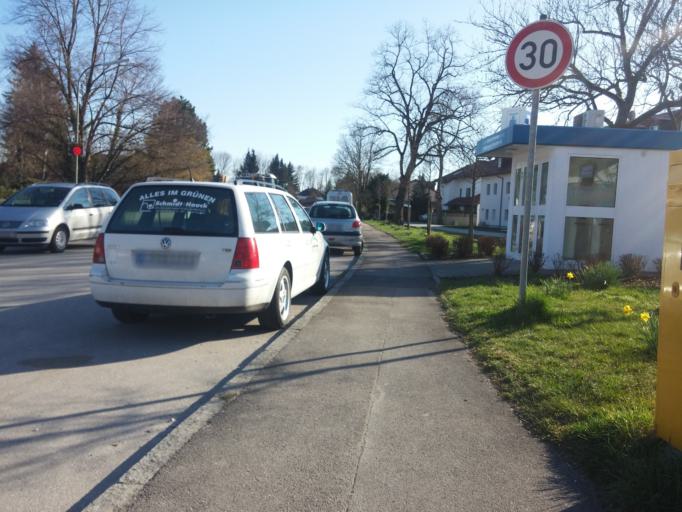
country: DE
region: Bavaria
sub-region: Upper Bavaria
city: Ismaning
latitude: 48.2527
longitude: 11.6945
